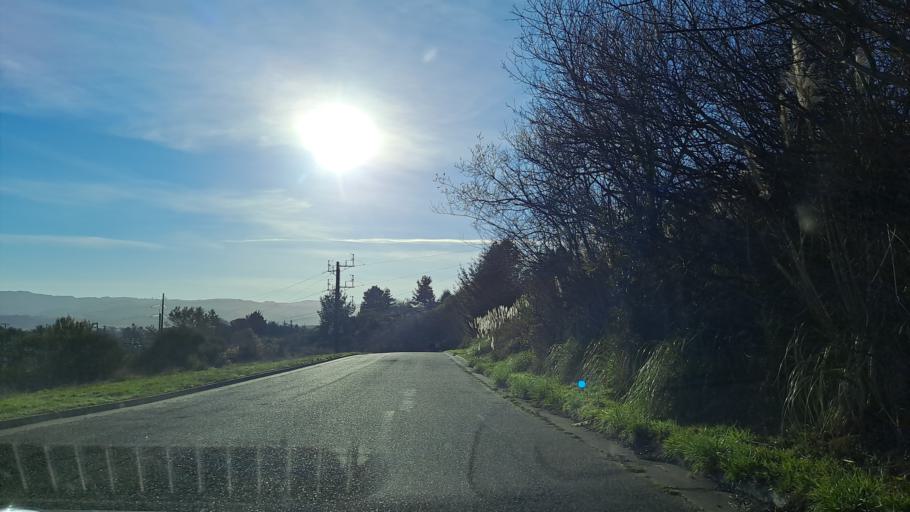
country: US
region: California
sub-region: Humboldt County
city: Fortuna
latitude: 40.5955
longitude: -124.1343
